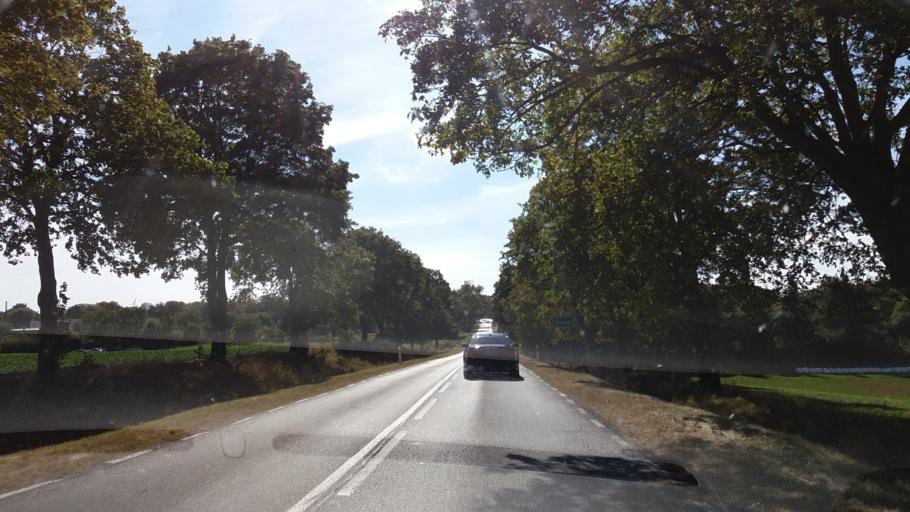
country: PL
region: Greater Poland Voivodeship
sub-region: Powiat miedzychodzki
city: Miedzychod
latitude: 52.5707
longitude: 15.8960
